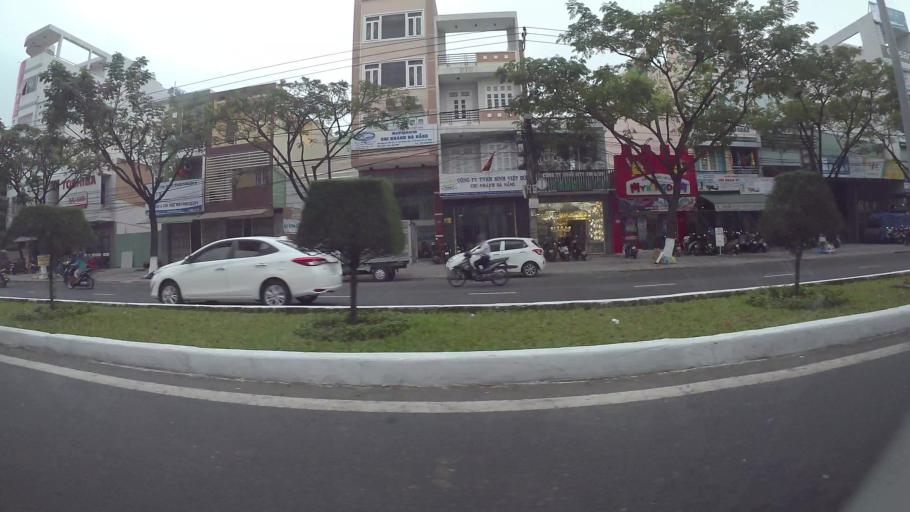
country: VN
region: Da Nang
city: Cam Le
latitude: 16.0415
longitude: 108.2105
